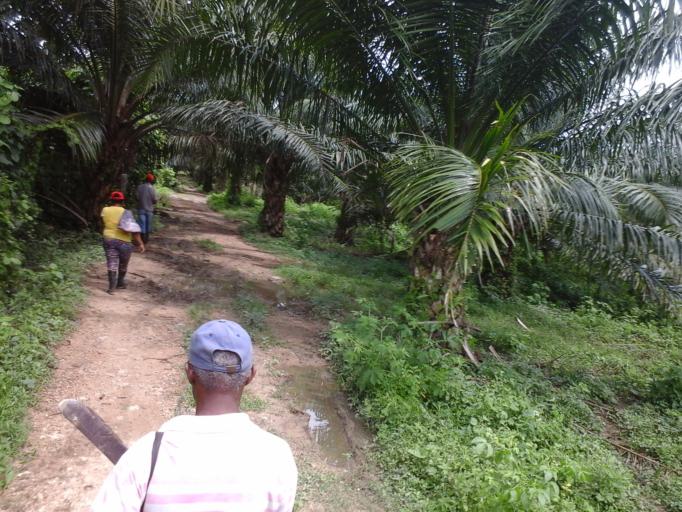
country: CO
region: Bolivar
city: San Pablo
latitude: 10.1608
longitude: -75.2754
